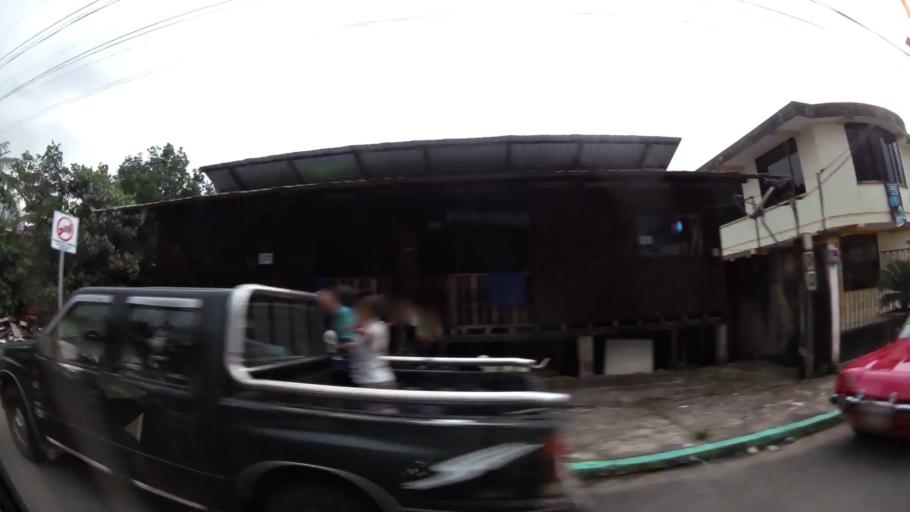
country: EC
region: Pastaza
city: Puyo
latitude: -1.4884
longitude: -78.0134
